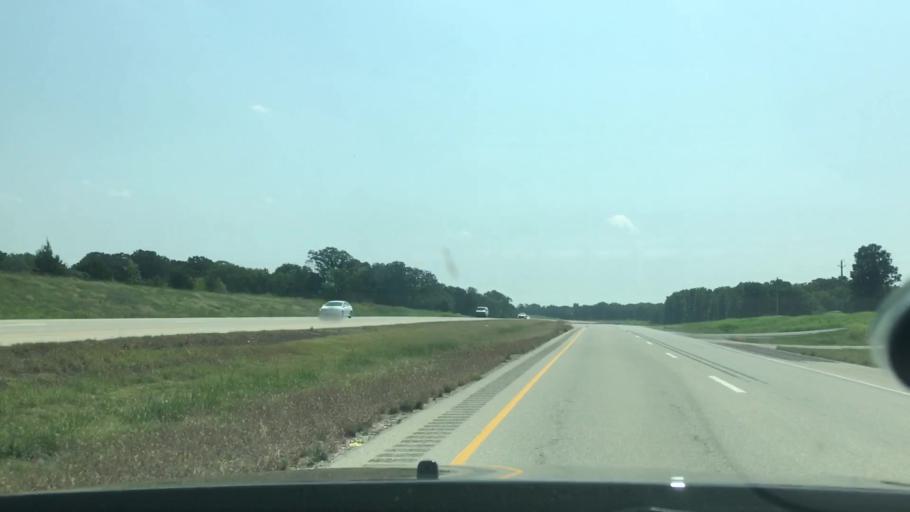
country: US
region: Oklahoma
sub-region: Atoka County
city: Atoka
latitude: 34.3214
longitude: -96.0381
